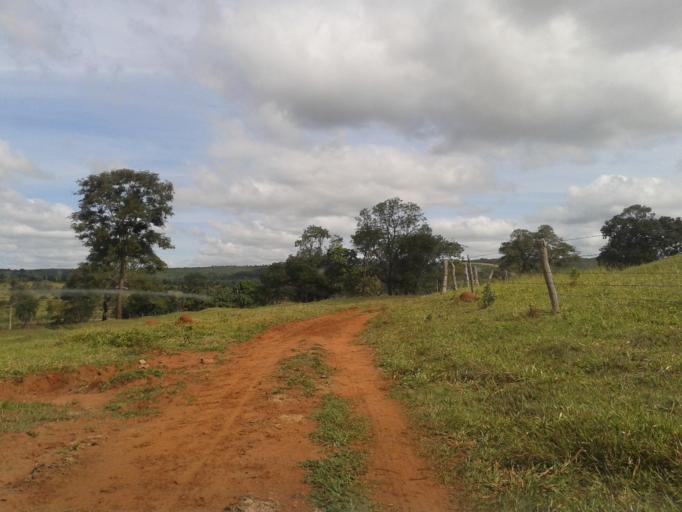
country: BR
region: Minas Gerais
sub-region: Campina Verde
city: Campina Verde
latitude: -19.4270
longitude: -49.7014
